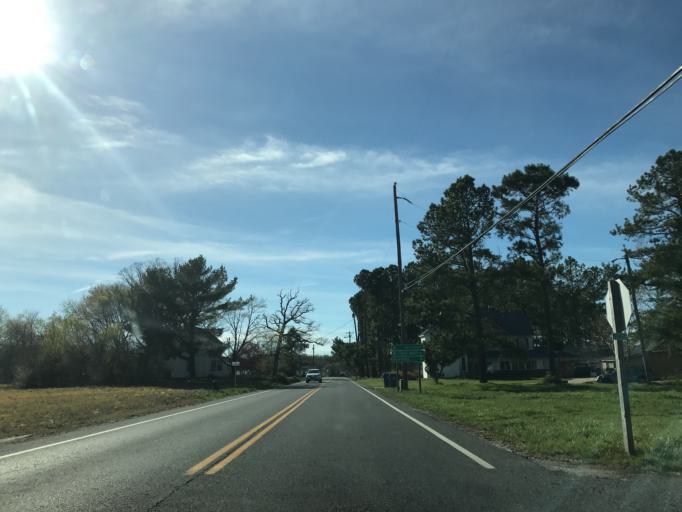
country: US
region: Maryland
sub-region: Caroline County
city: Greensboro
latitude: 39.0369
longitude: -75.7828
